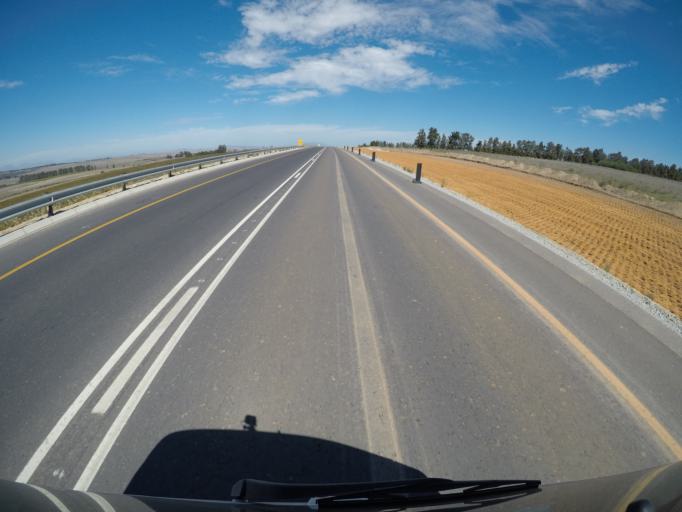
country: ZA
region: Western Cape
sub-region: West Coast District Municipality
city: Malmesbury
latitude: -33.4989
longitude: 18.6651
